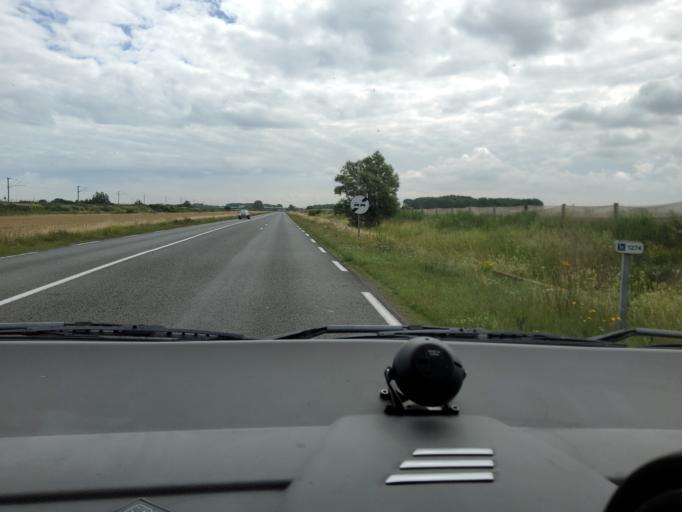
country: FR
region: Nord-Pas-de-Calais
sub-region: Departement du Nord
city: Loon-Plage
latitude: 50.9958
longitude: 2.1784
